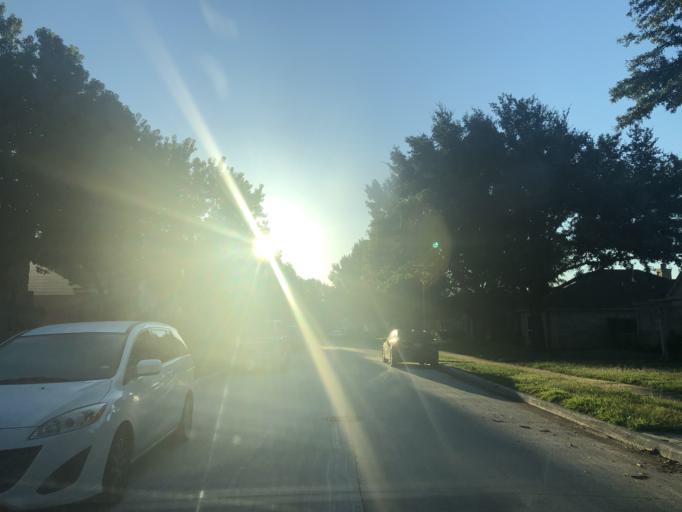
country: US
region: Texas
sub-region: Dallas County
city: Grand Prairie
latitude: 32.6661
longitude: -96.9930
